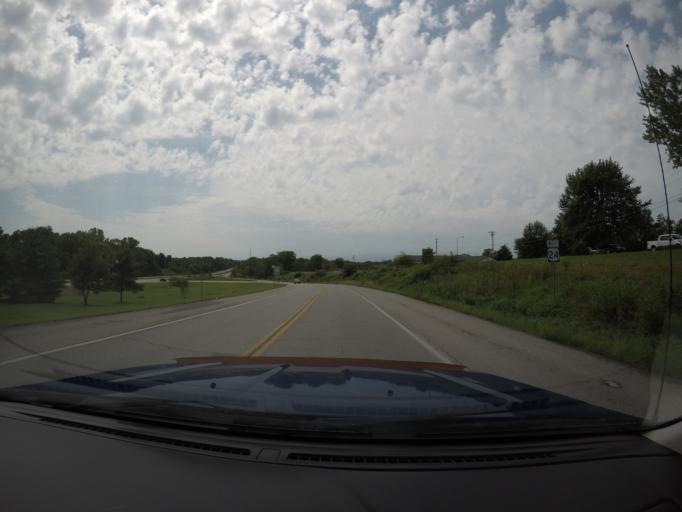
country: US
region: Missouri
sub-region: Lafayette County
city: Lexington
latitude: 39.1645
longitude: -93.8799
